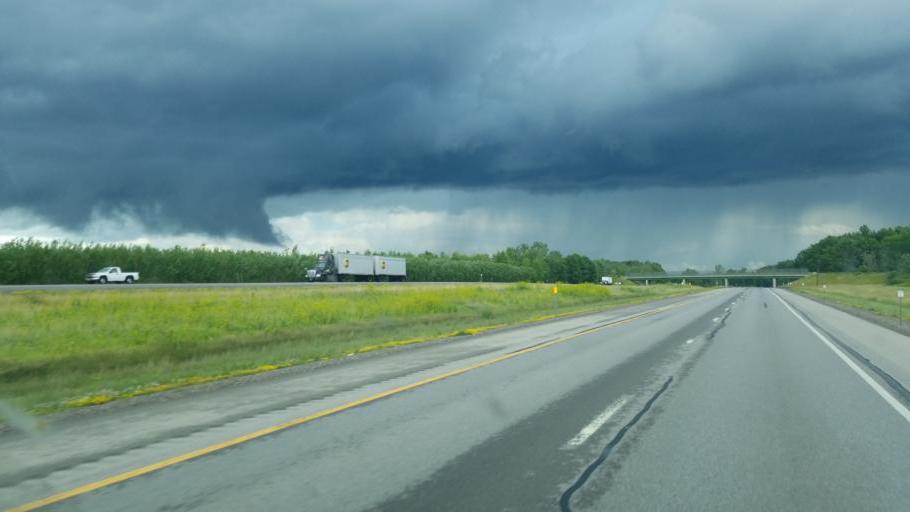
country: US
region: New York
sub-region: Erie County
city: Angola
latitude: 42.5993
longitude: -79.0355
